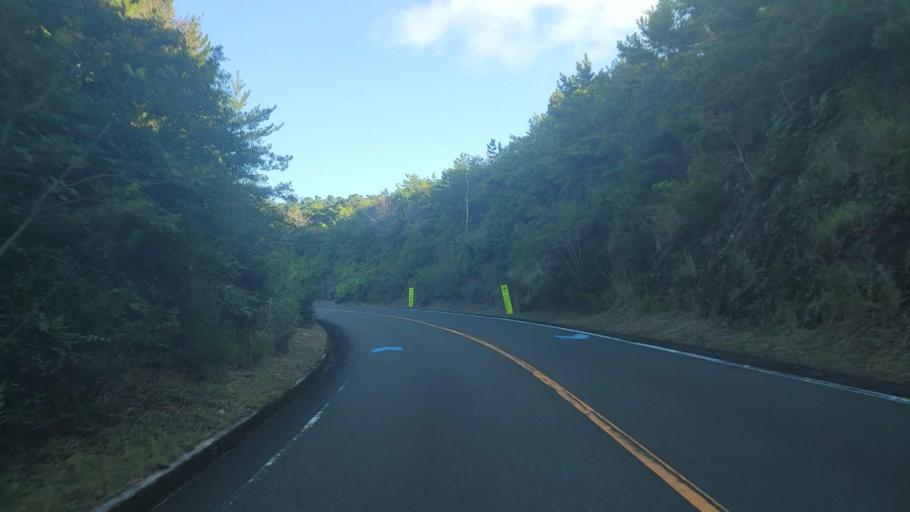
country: JP
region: Mie
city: Toba
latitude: 34.3930
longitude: 136.8608
